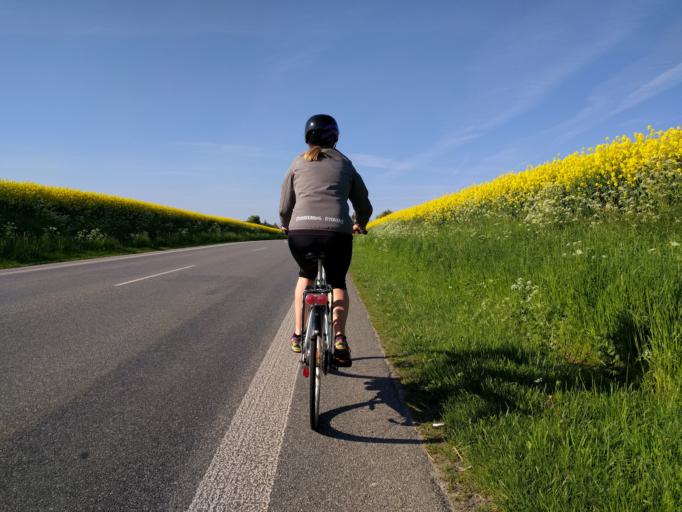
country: DK
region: Zealand
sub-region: Guldborgsund Kommune
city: Stubbekobing
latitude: 54.8751
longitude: 12.0269
